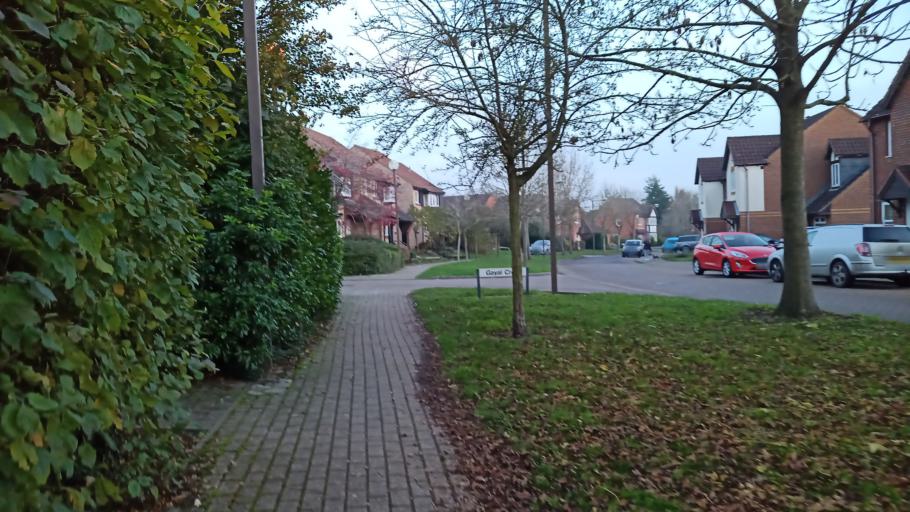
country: GB
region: England
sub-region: Milton Keynes
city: Shenley Church End
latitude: 52.0132
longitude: -0.7822
